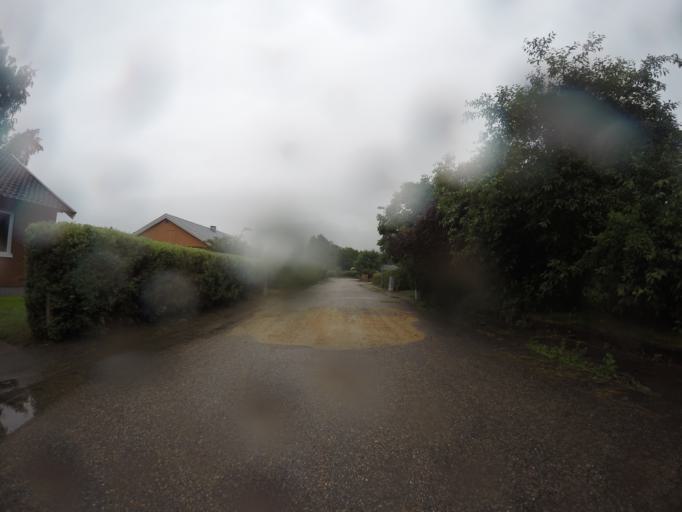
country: SE
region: Vaestra Goetaland
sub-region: Trollhattan
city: Sjuntorp
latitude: 58.1833
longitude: 12.2243
